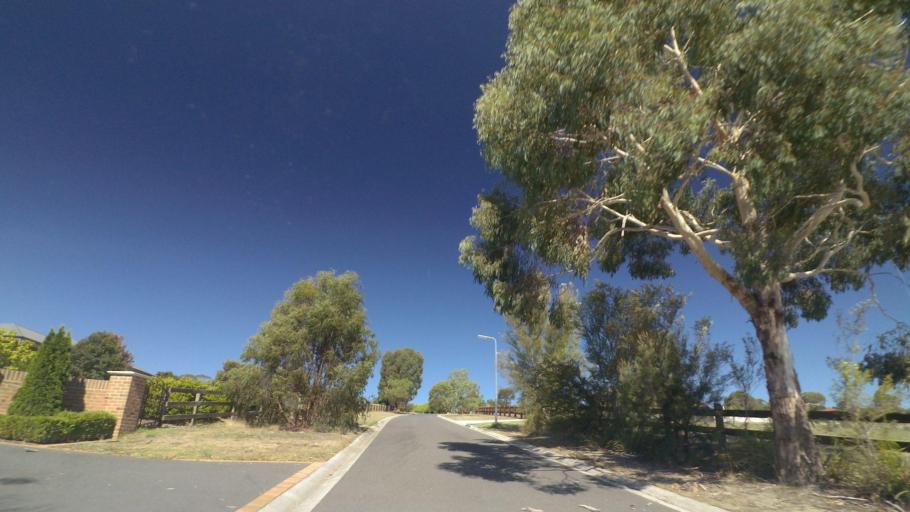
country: AU
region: Victoria
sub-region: Yarra Ranges
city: Chirnside Park
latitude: -37.7485
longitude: 145.3146
